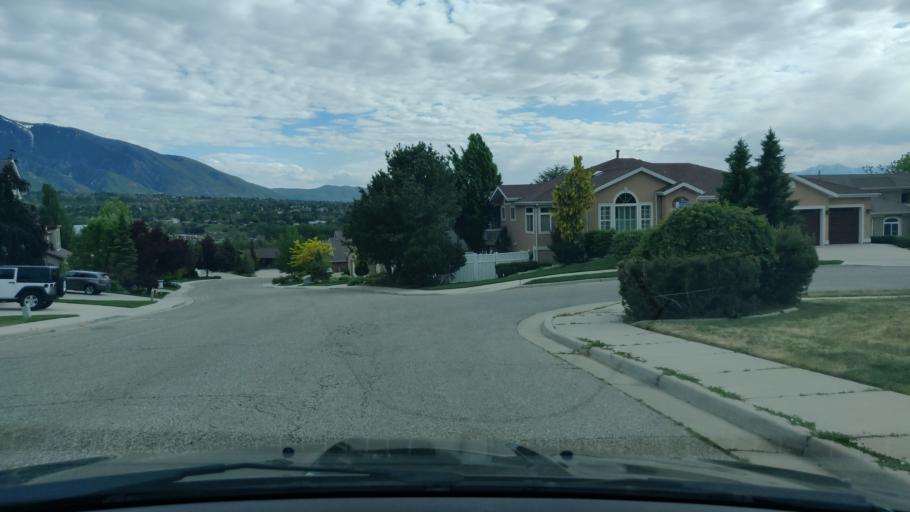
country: US
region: Utah
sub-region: Salt Lake County
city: Cottonwood Heights
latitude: 40.6084
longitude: -111.8136
